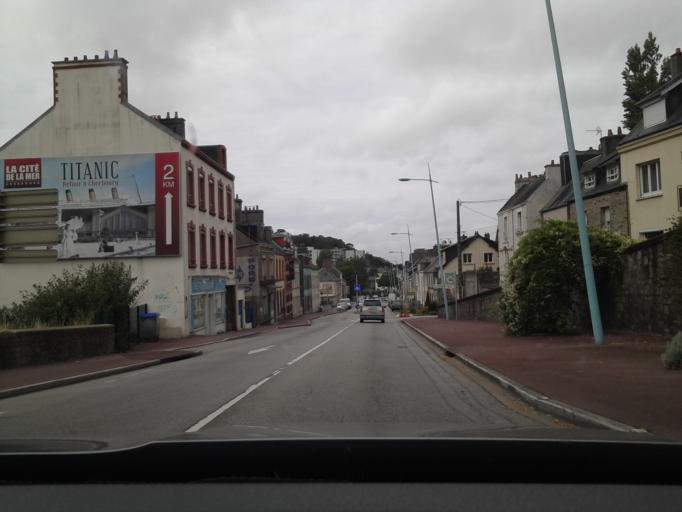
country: FR
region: Lower Normandy
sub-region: Departement de la Manche
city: Cherbourg-Octeville
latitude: 49.6261
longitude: -1.6171
